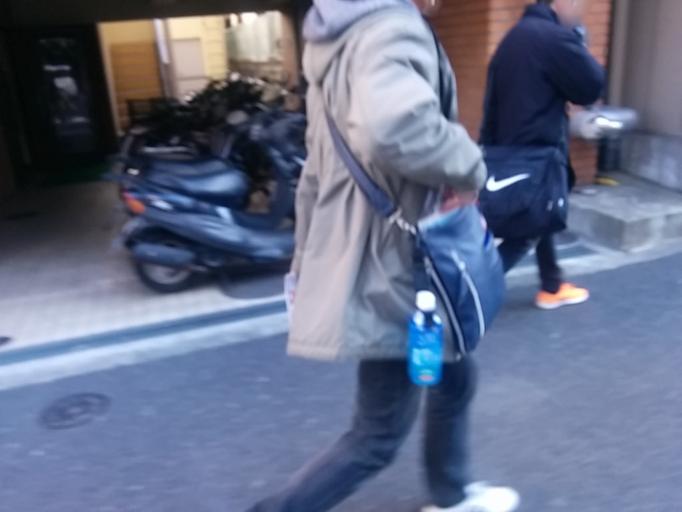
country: JP
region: Tokyo
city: Tokyo
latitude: 35.7302
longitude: 139.7511
